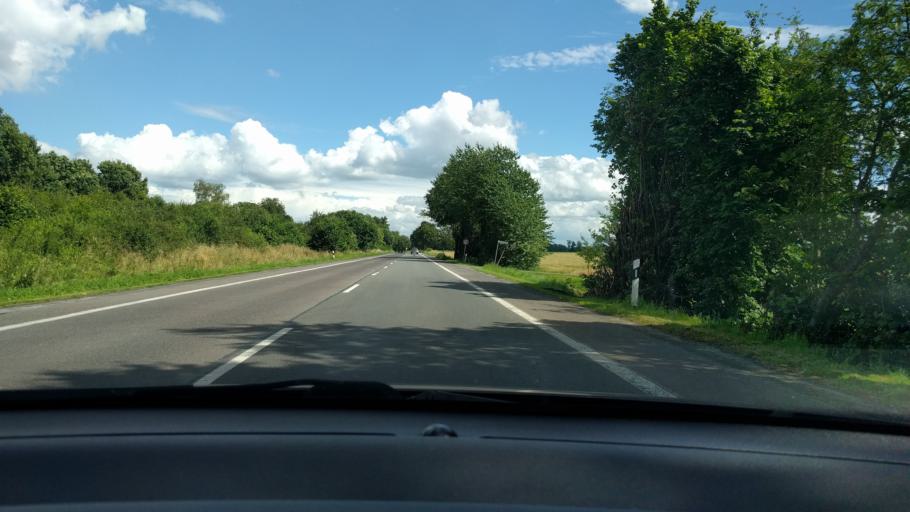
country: DE
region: North Rhine-Westphalia
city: Olfen
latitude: 51.6887
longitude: 7.3181
